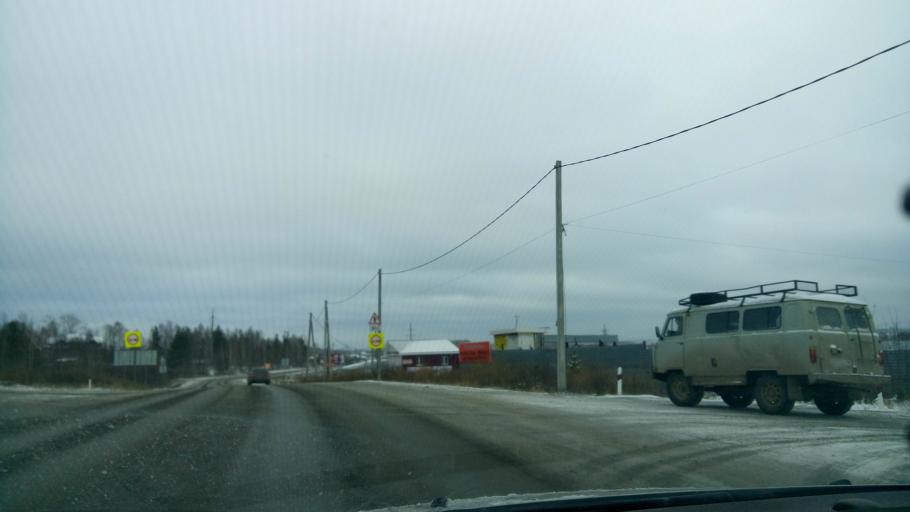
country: RU
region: Sverdlovsk
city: Polevskoy
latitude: 56.4607
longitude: 60.2147
